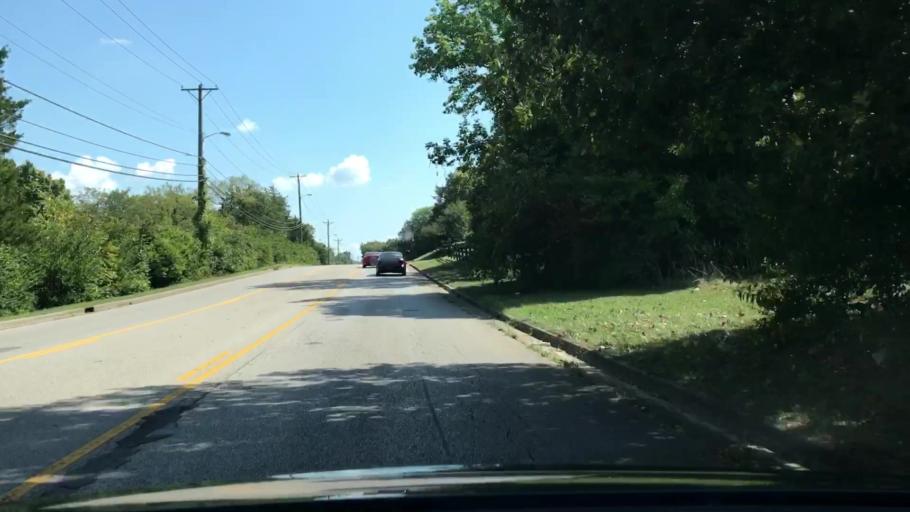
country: US
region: Tennessee
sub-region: Williamson County
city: Brentwood Estates
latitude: 36.0329
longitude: -86.7724
